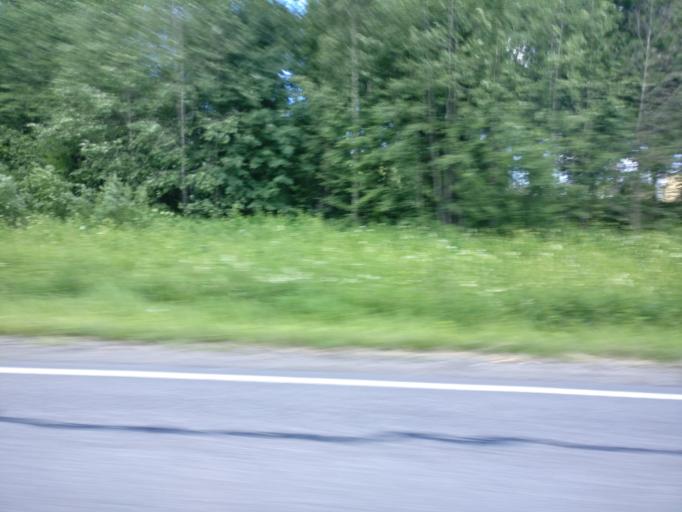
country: FI
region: Southern Savonia
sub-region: Savonlinna
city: Kerimaeki
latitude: 61.8275
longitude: 29.2377
